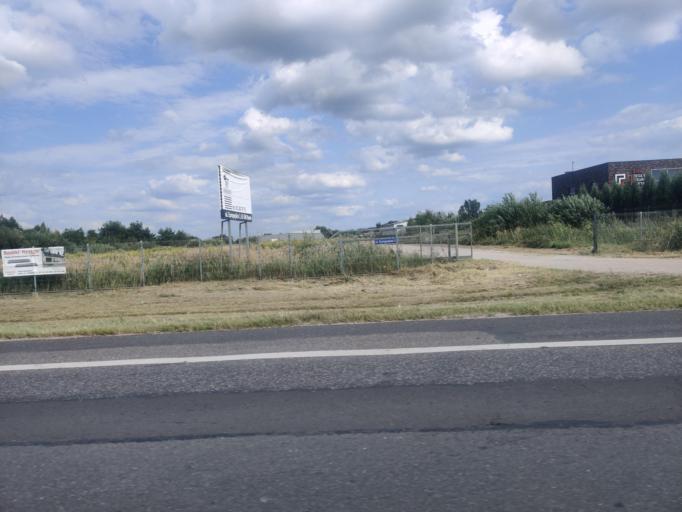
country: PL
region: Greater Poland Voivodeship
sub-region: Konin
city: Konin
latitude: 52.1962
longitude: 18.2680
